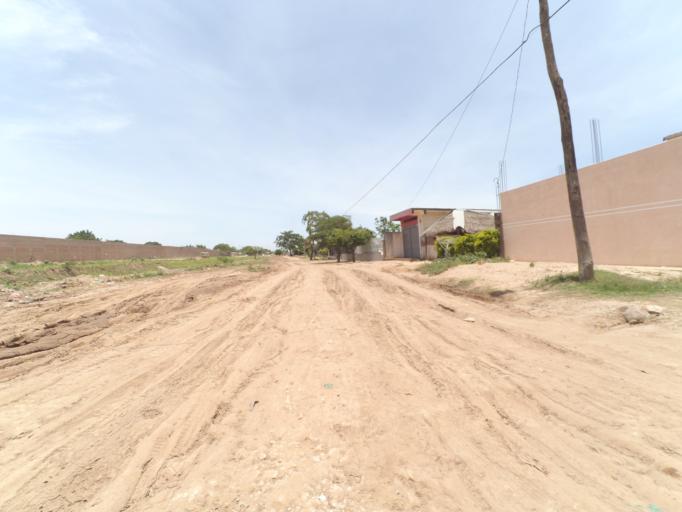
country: BO
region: Santa Cruz
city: Santa Cruz de la Sierra
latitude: -17.8281
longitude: -63.2438
